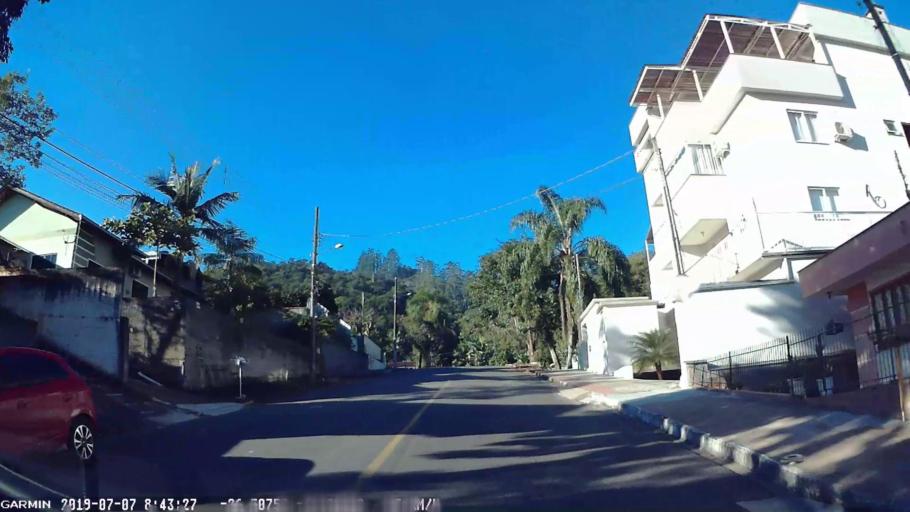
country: BR
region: Santa Catarina
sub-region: Jaragua Do Sul
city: Jaragua do Sul
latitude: -26.5077
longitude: -49.0925
